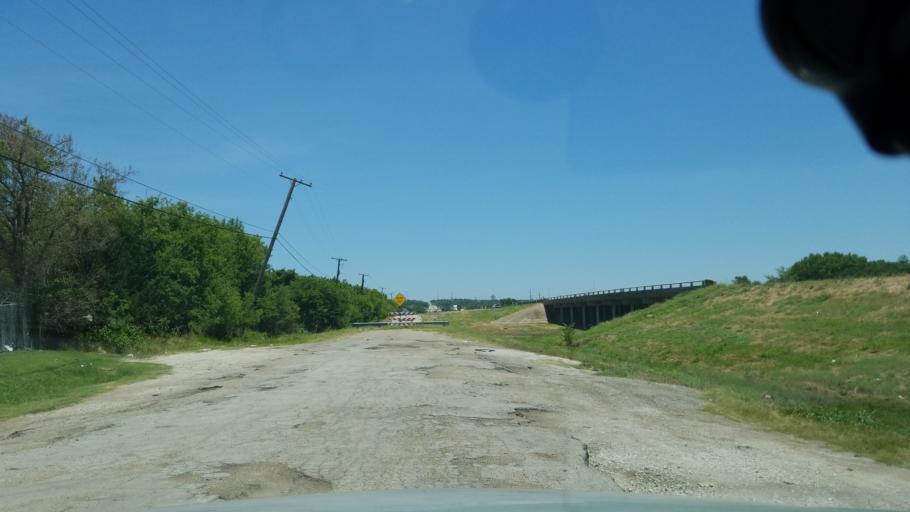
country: US
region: Texas
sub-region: Dallas County
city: Cockrell Hill
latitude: 32.7499
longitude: -96.9380
